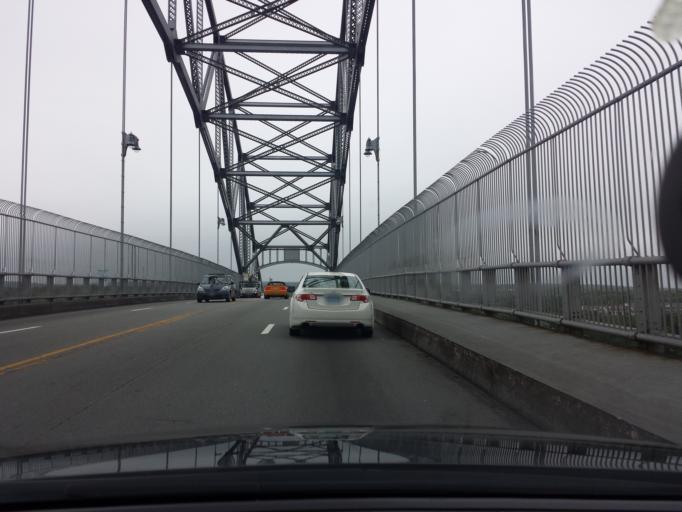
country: US
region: Massachusetts
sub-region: Barnstable County
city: Bourne
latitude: 41.7480
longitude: -70.5897
